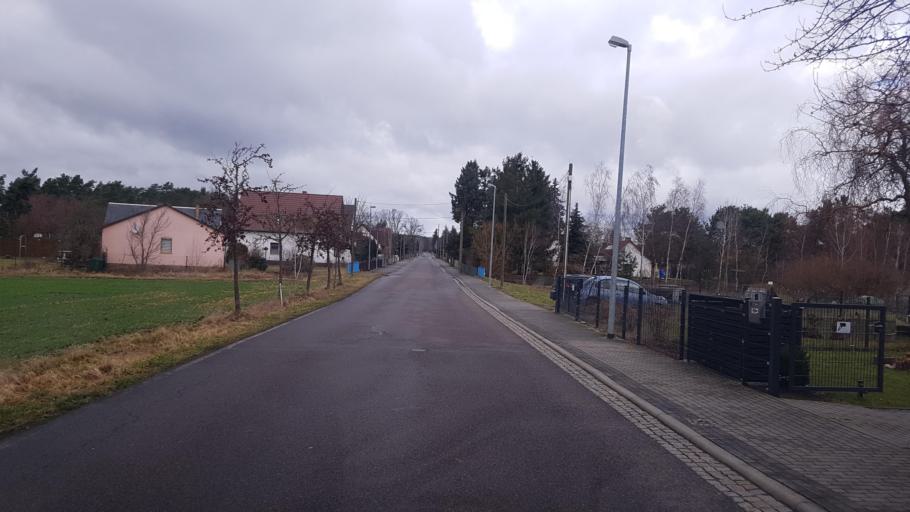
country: DE
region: Brandenburg
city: Schipkau
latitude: 51.5465
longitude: 13.9235
